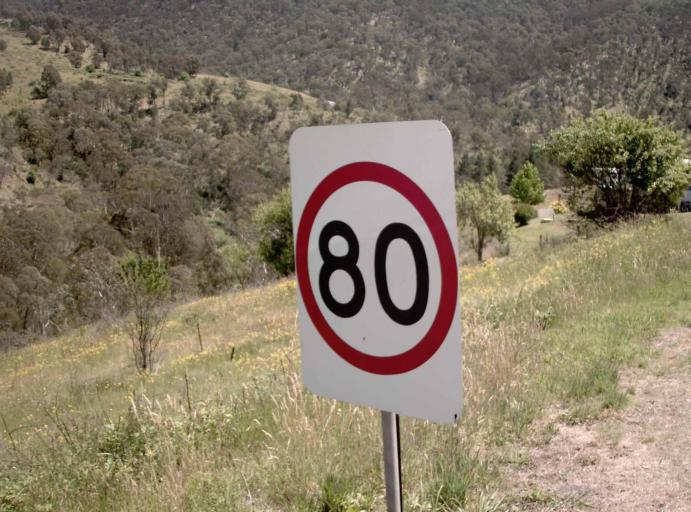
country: AU
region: Victoria
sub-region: Alpine
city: Mount Beauty
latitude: -37.1059
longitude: 147.5814
